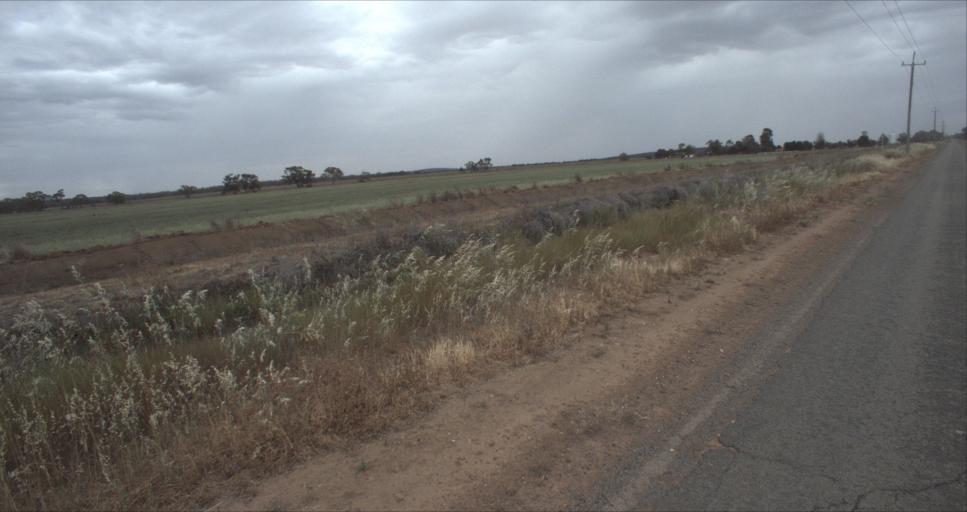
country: AU
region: New South Wales
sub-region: Leeton
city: Leeton
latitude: -34.4264
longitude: 146.3375
